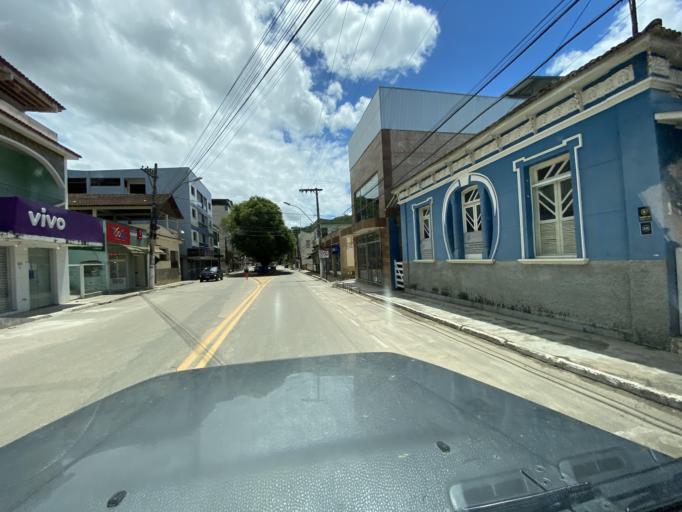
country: BR
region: Espirito Santo
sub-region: Jeronimo Monteiro
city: Jeronimo Monteiro
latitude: -20.7882
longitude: -41.3931
